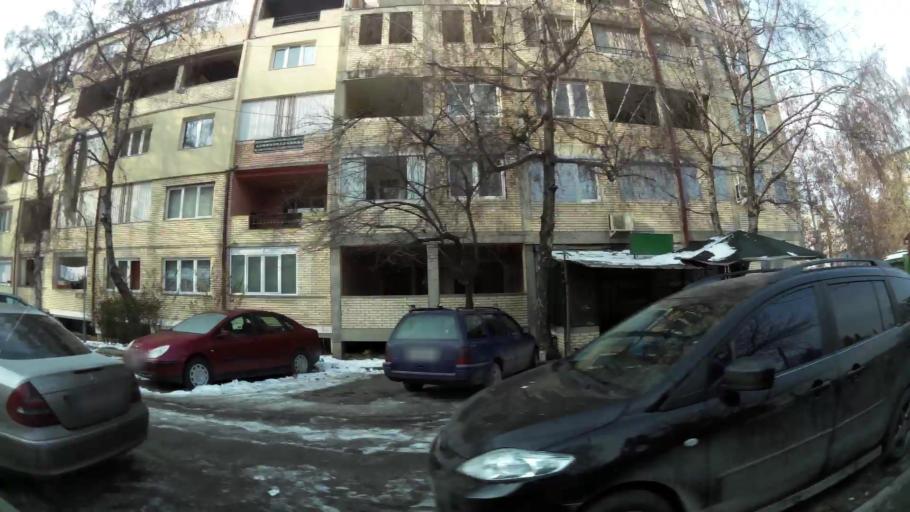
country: MK
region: Cair
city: Cair
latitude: 42.0187
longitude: 21.4325
